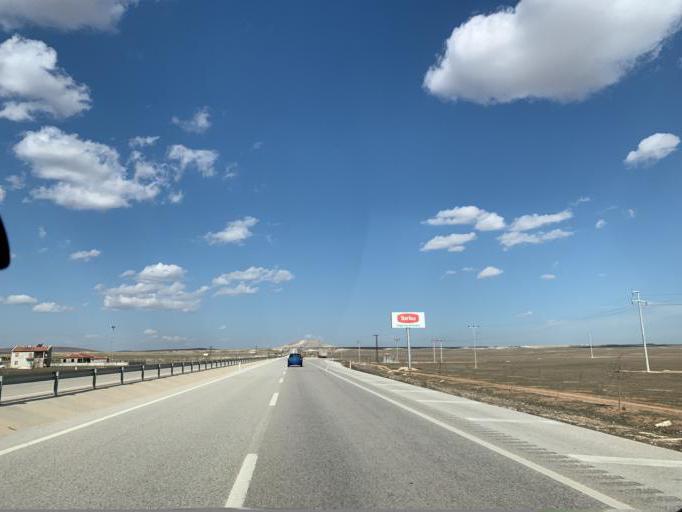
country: TR
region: Konya
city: Cihanbeyli
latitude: 38.5168
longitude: 32.8603
